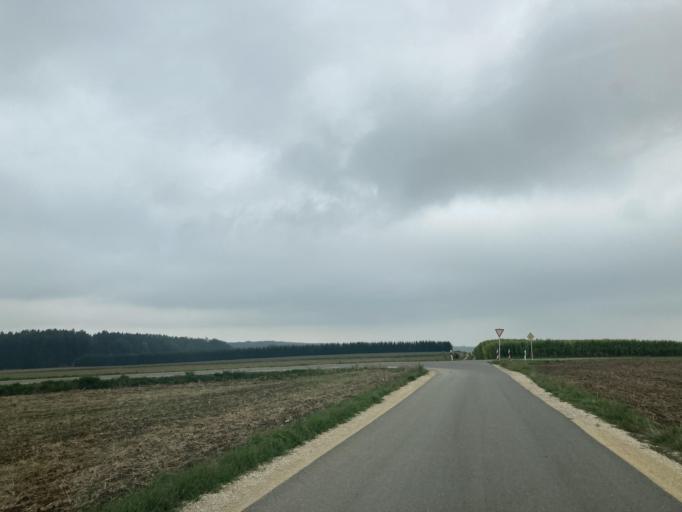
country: DE
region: Bavaria
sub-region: Swabia
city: Medlingen
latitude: 48.5813
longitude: 10.3089
